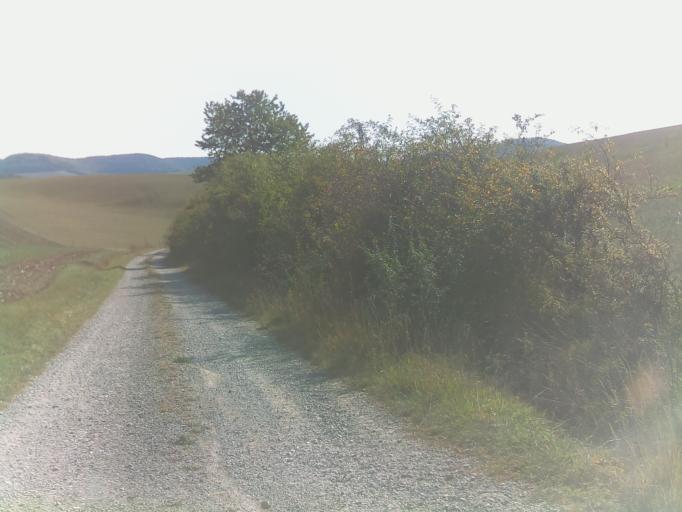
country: DE
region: Thuringia
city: Henneberg
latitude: 50.5262
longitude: 10.3276
